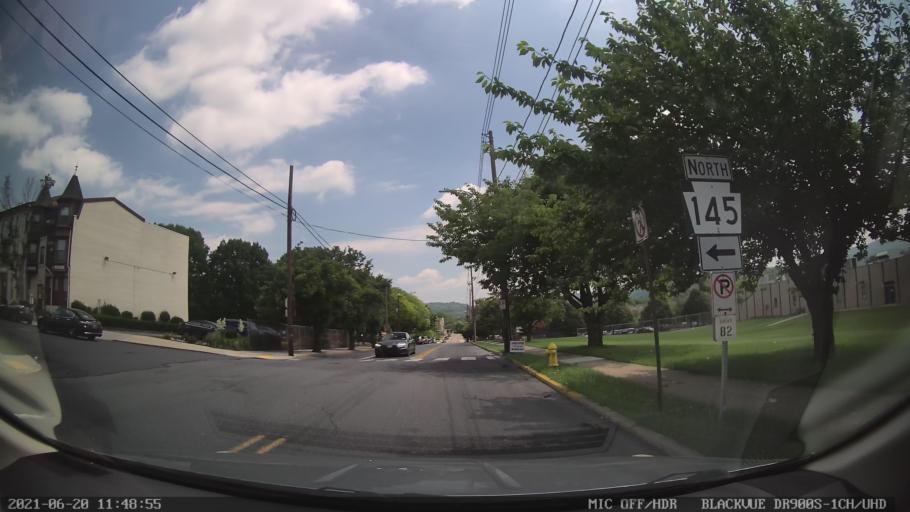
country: US
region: Pennsylvania
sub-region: Lehigh County
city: Allentown
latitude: 40.5999
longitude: -75.4686
